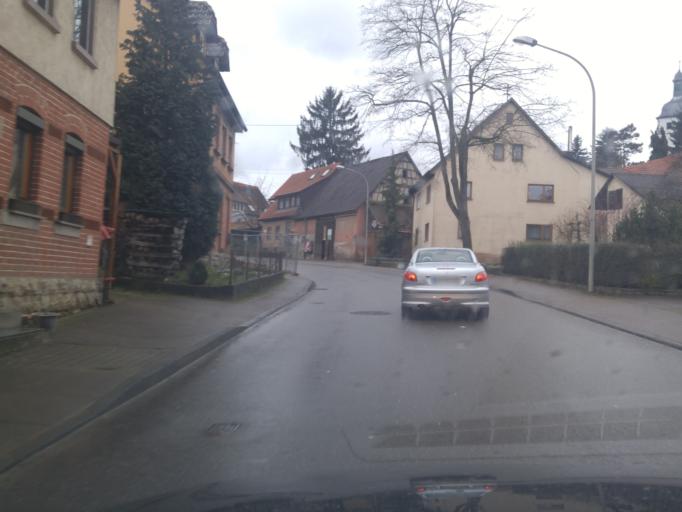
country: DE
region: Baden-Wuerttemberg
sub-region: Regierungsbezirk Stuttgart
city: Erdmannhausen
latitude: 48.9426
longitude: 9.2980
